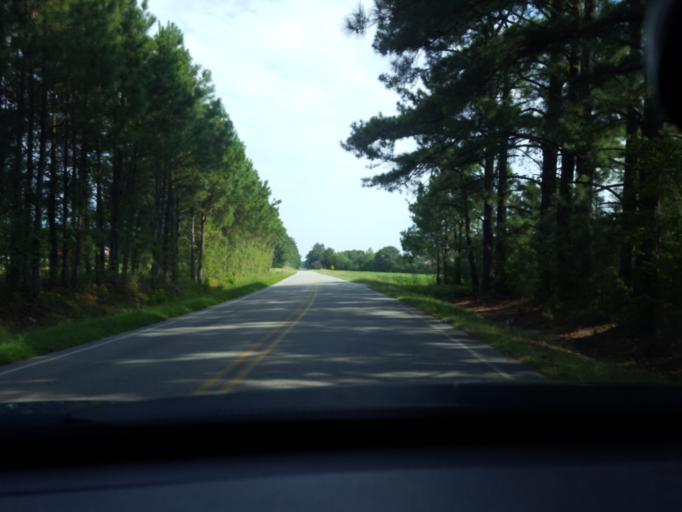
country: US
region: North Carolina
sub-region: Washington County
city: Plymouth
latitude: 35.8790
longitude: -76.7123
